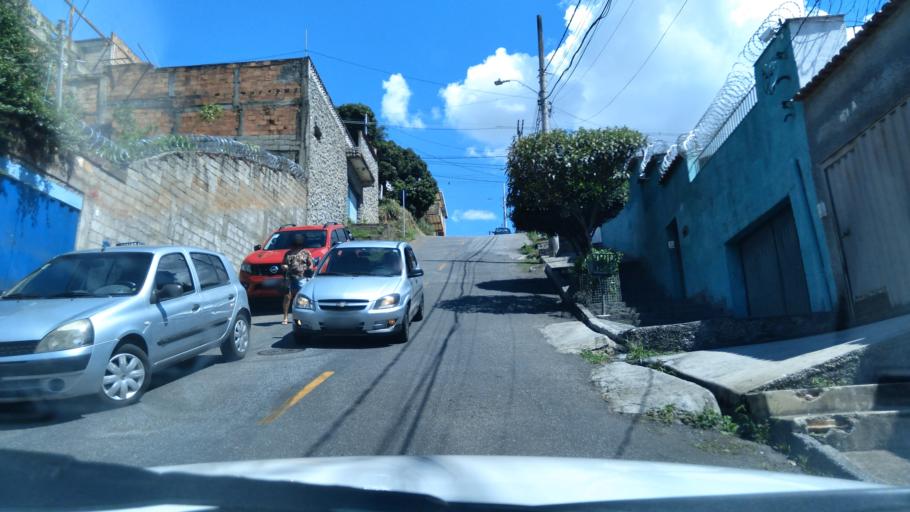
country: BR
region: Minas Gerais
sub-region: Belo Horizonte
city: Belo Horizonte
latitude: -19.8747
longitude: -43.9135
